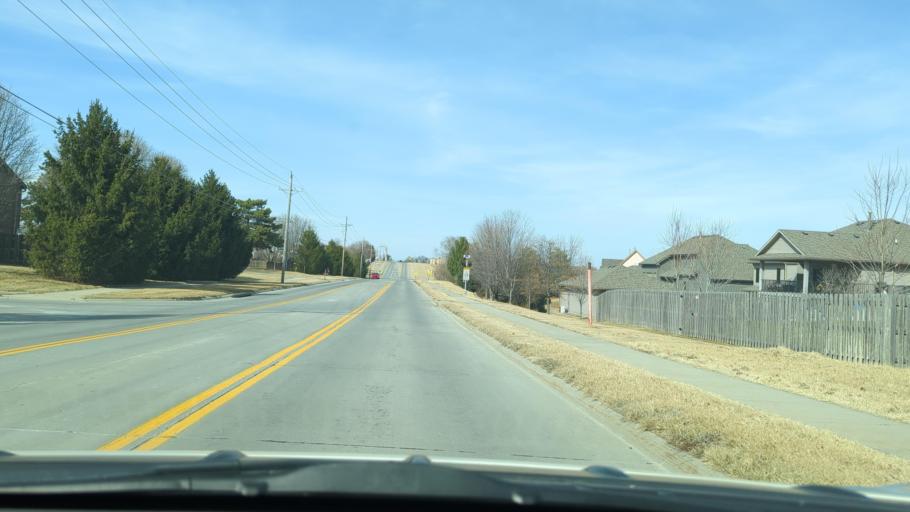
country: US
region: Nebraska
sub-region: Sarpy County
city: Papillion
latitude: 41.1338
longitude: -96.0524
